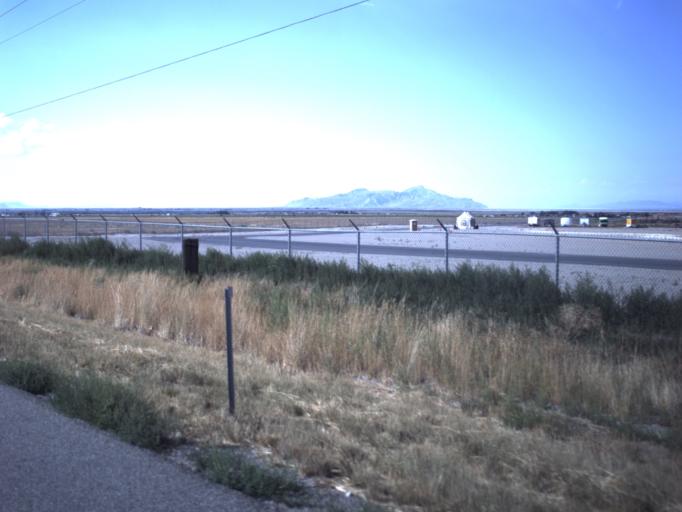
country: US
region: Utah
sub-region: Tooele County
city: Grantsville
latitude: 40.5762
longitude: -112.3884
